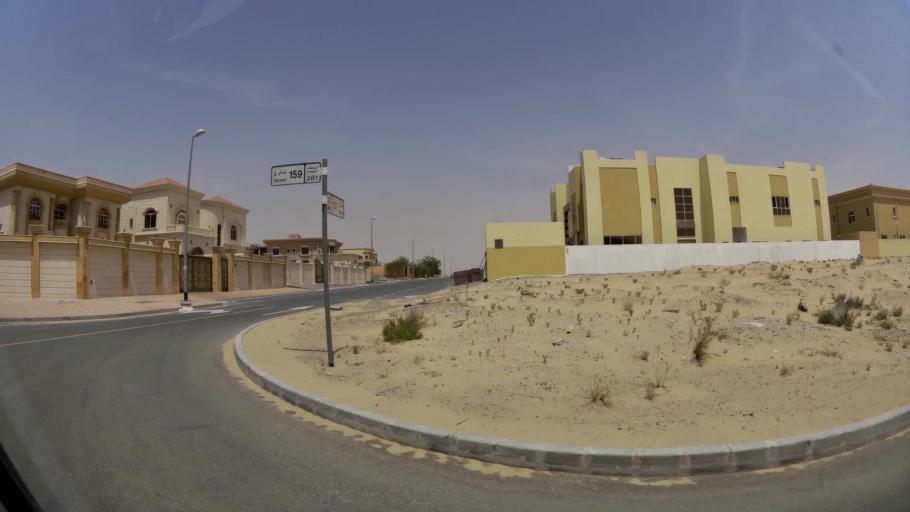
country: AE
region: Ash Shariqah
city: Sharjah
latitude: 25.2478
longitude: 55.5052
